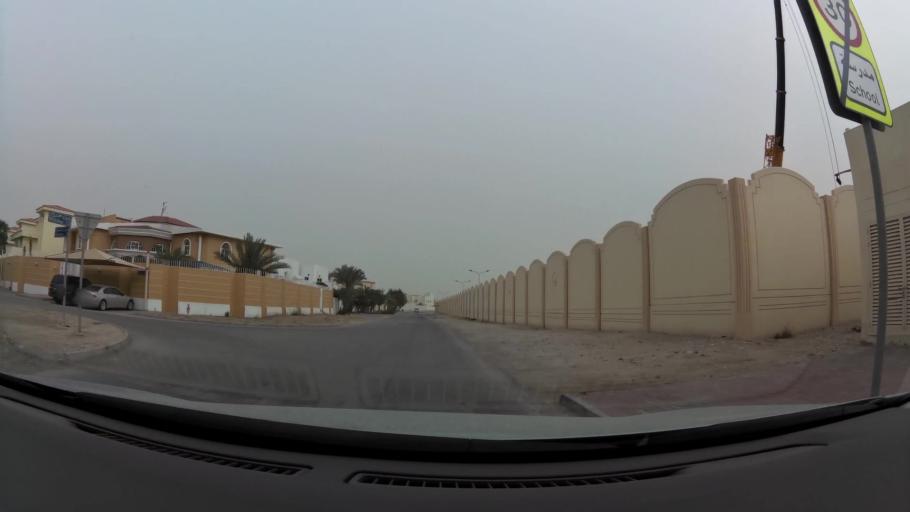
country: QA
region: Baladiyat ad Dawhah
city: Doha
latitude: 25.2574
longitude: 51.4906
